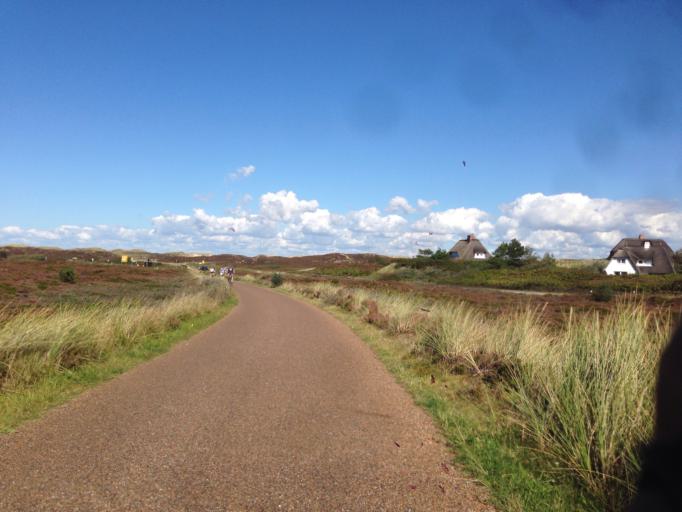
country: DE
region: Schleswig-Holstein
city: List
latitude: 55.0002
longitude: 8.3779
